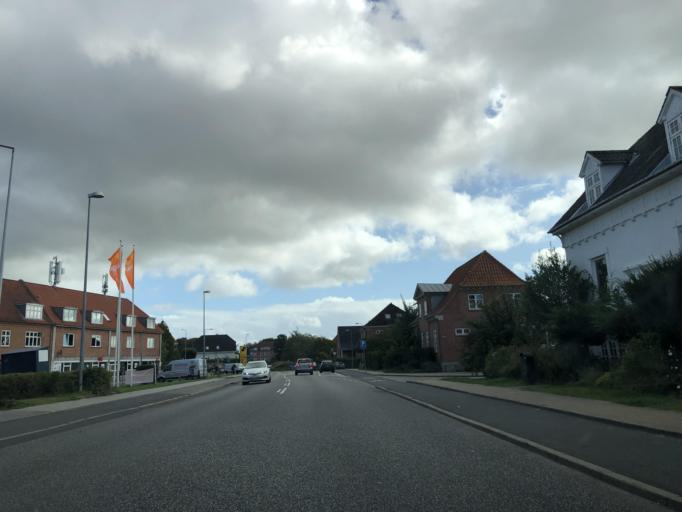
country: DK
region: Central Jutland
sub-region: Randers Kommune
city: Randers
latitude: 56.4685
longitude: 10.0193
